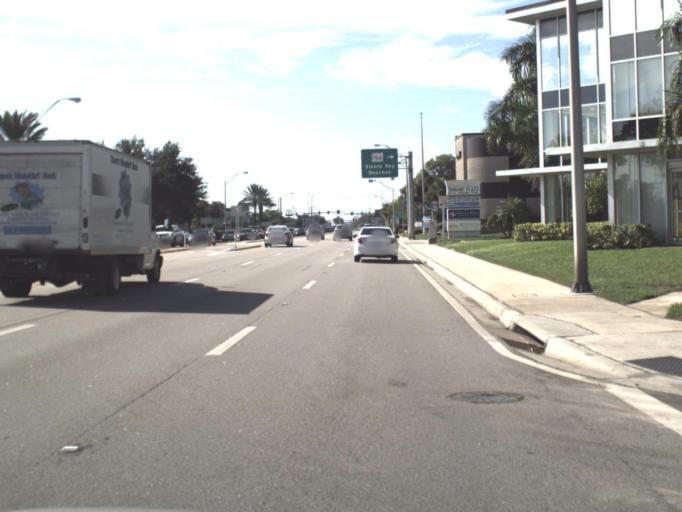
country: US
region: Florida
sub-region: Sarasota County
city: South Sarasota
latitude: 27.3021
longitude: -82.5305
